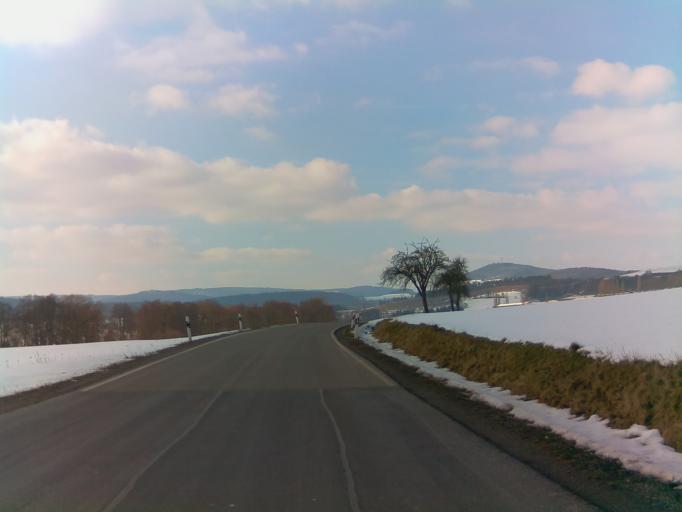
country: DE
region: Thuringia
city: Oberkatz
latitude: 50.5657
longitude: 10.2268
